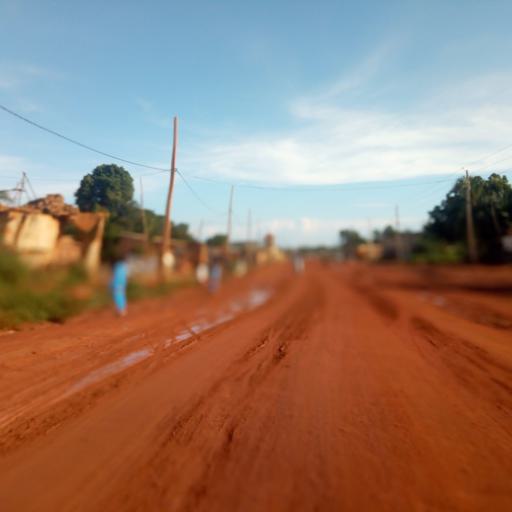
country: BJ
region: Atlantique
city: Hevie
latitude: 6.4222
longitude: 2.2601
